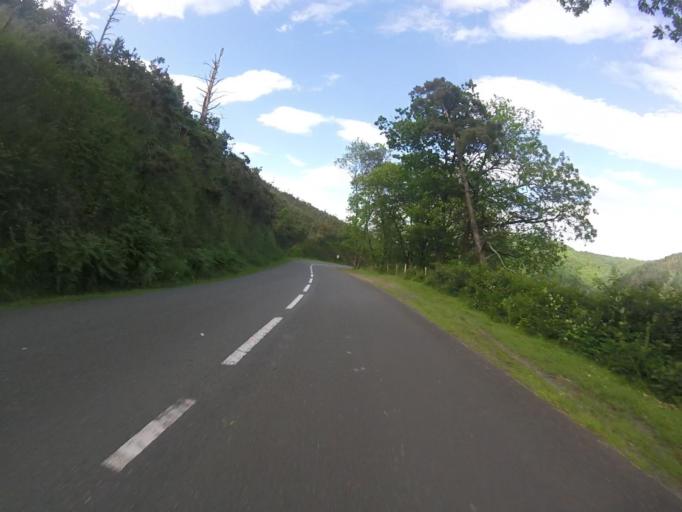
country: ES
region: Navarre
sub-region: Provincia de Navarra
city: Arano
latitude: 43.2495
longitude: -1.8462
